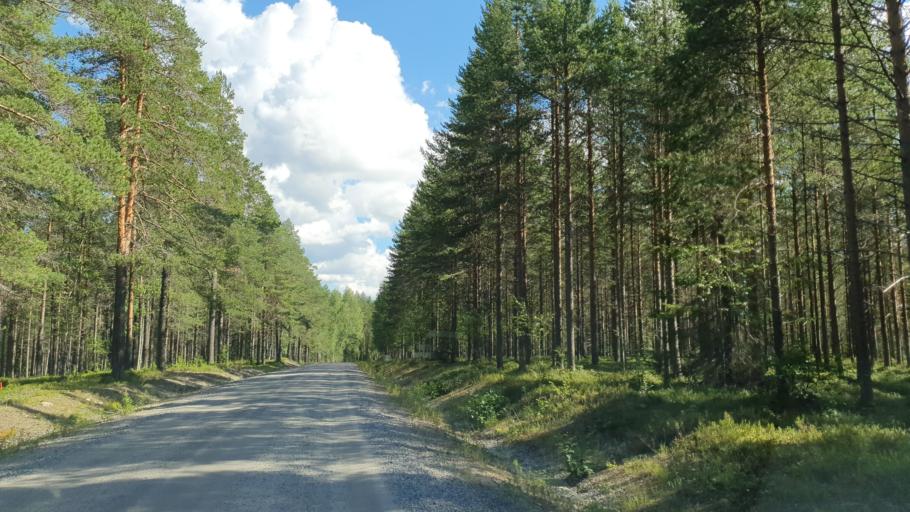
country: FI
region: Kainuu
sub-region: Kehys-Kainuu
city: Kuhmo
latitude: 64.1072
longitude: 29.3917
